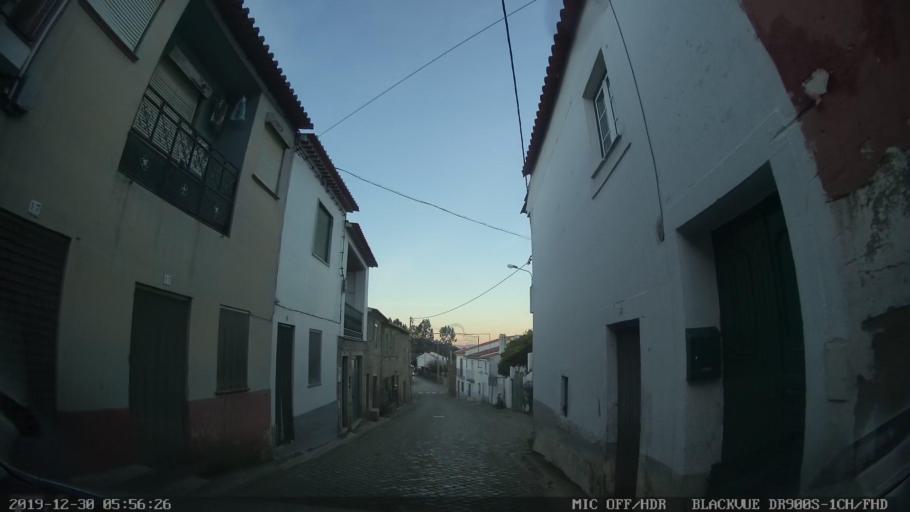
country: PT
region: Castelo Branco
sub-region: Idanha-A-Nova
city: Idanha-a-Nova
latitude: 40.0256
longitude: -7.2403
